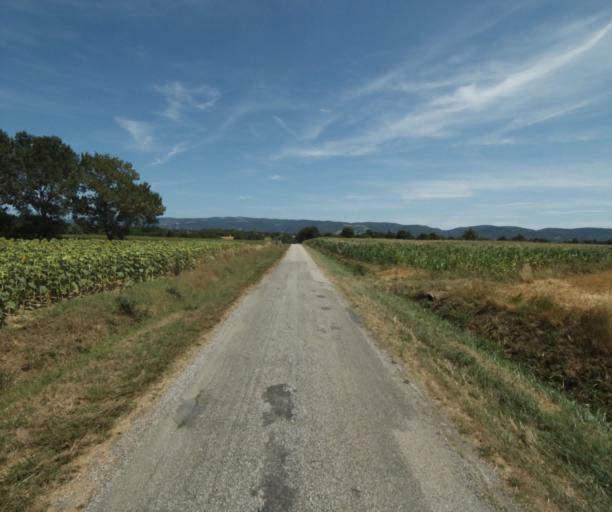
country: FR
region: Midi-Pyrenees
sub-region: Departement de la Haute-Garonne
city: Revel
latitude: 43.4962
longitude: 2.0135
